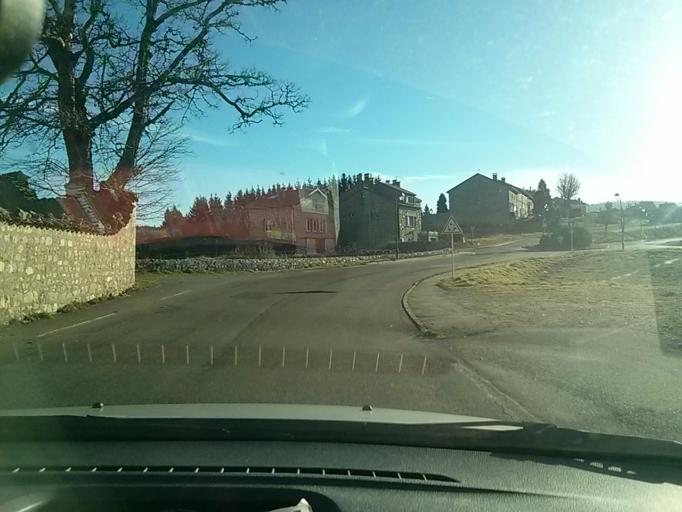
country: FR
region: Rhone-Alpes
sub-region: Departement de la Loire
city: Bourg-Argental
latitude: 45.3708
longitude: 4.5120
